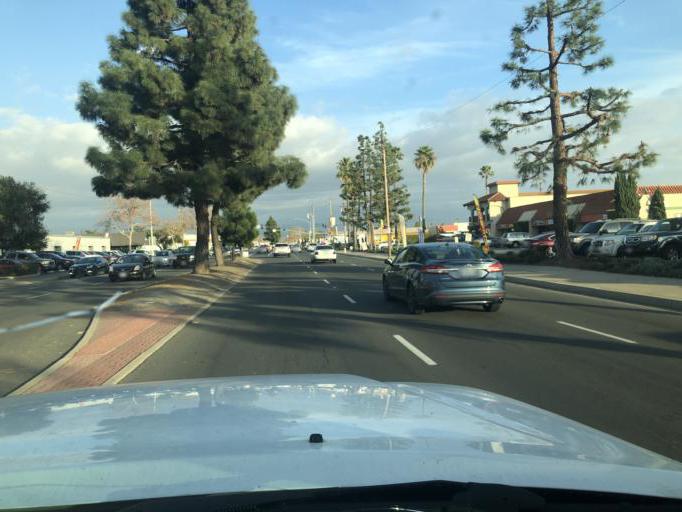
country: US
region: California
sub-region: Orange County
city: Santa Ana
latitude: 33.7268
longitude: -117.8525
